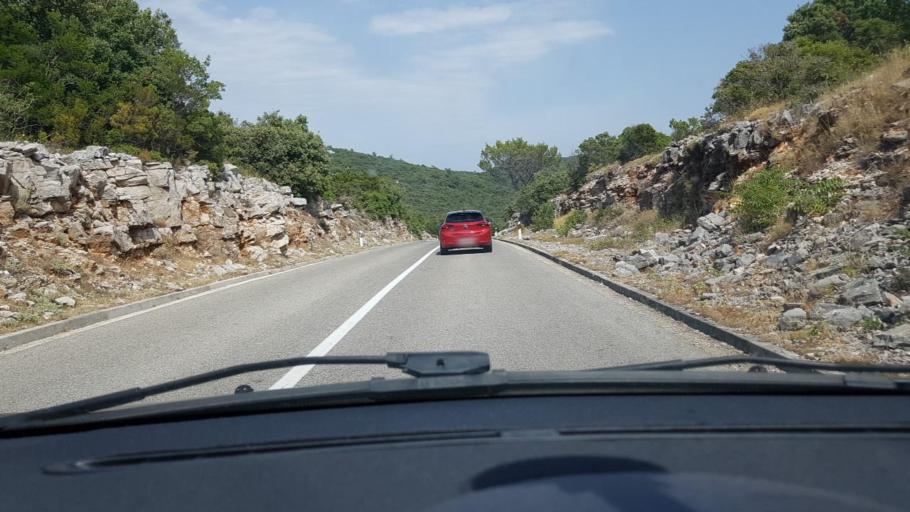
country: HR
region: Dubrovacko-Neretvanska
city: Smokvica
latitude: 42.9489
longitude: 16.9830
